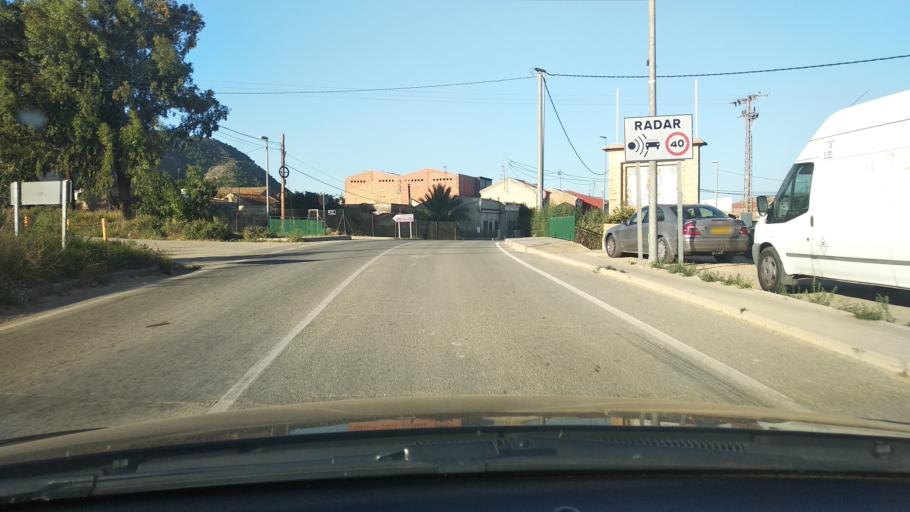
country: ES
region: Murcia
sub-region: Murcia
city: Beniel
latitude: 37.9960
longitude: -1.0293
